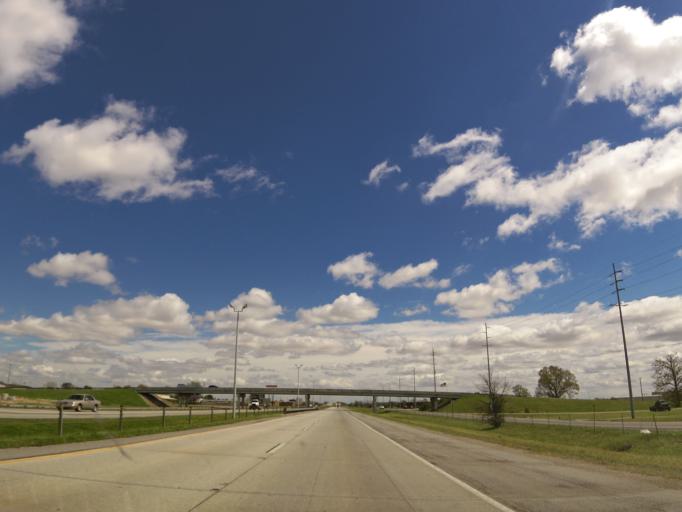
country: US
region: Arkansas
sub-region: Craighead County
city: Jonesboro
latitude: 35.8069
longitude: -90.6535
